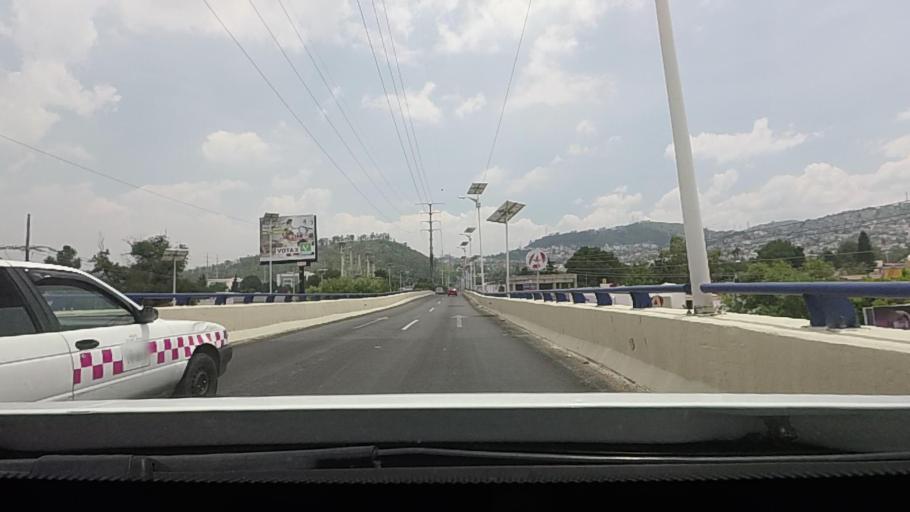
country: MX
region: Mexico
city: Naucalpan de Juarez
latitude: 19.4919
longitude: -99.2545
